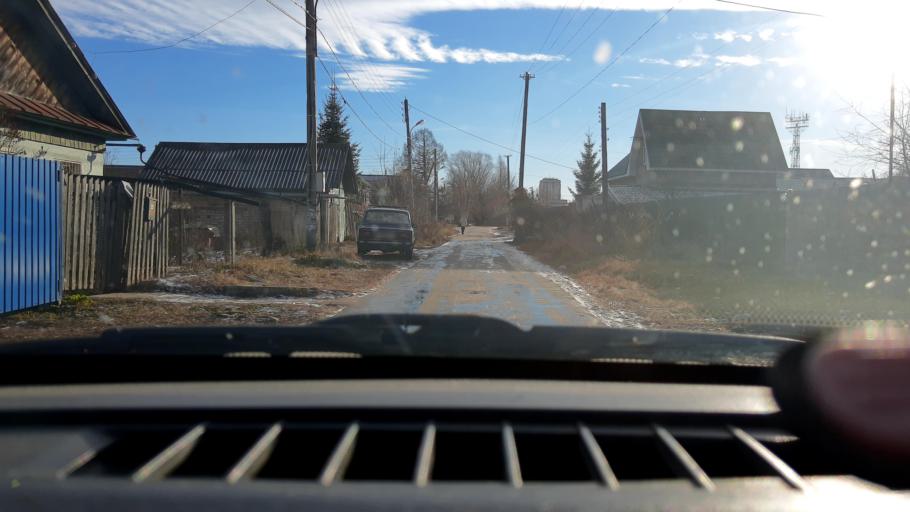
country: RU
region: Nizjnij Novgorod
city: Gorbatovka
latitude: 56.2966
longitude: 43.8468
